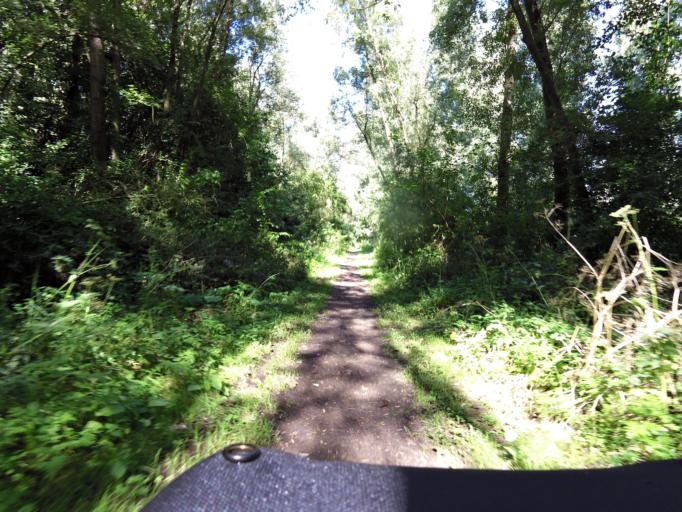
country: NL
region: South Holland
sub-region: Gemeente Dordrecht
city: Dordrecht
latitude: 51.7613
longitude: 4.6899
